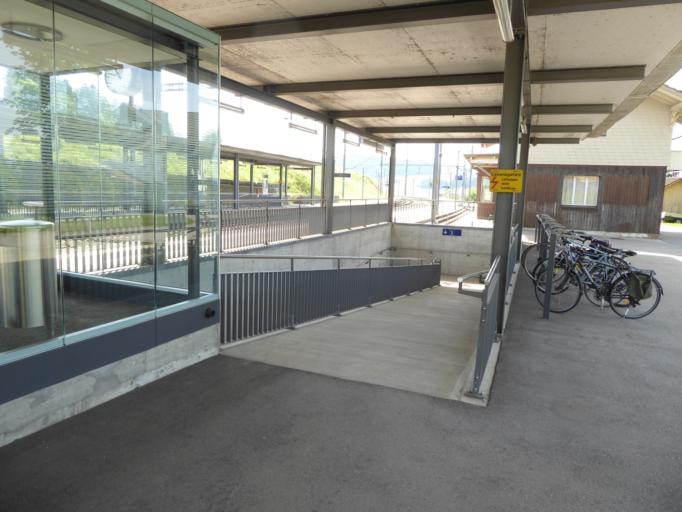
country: CH
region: Bern
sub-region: Bern-Mittelland District
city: Taegertschi
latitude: 46.8824
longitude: 7.5808
